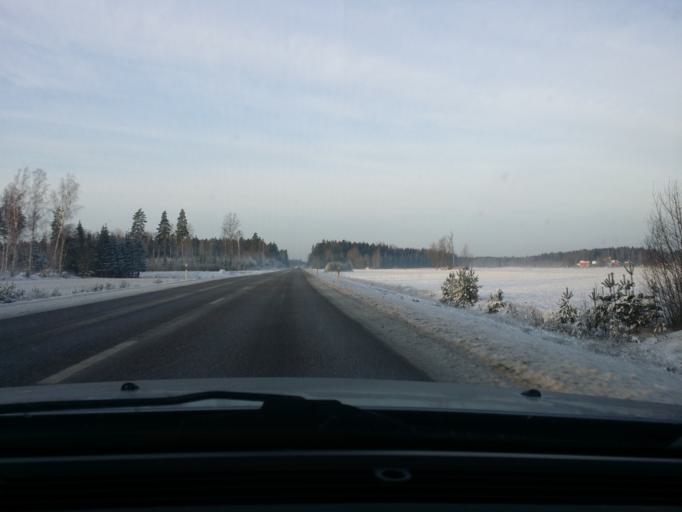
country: SE
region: OErebro
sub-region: Lindesbergs Kommun
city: Frovi
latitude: 59.4609
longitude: 15.4340
